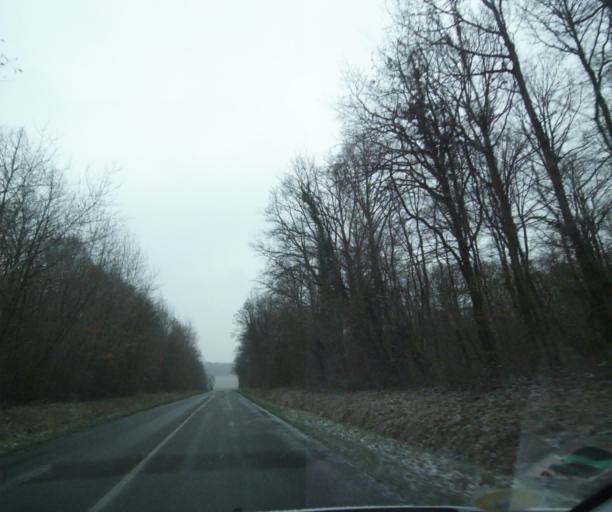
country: FR
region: Champagne-Ardenne
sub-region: Departement de la Haute-Marne
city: Wassy
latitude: 48.4723
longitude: 5.0207
